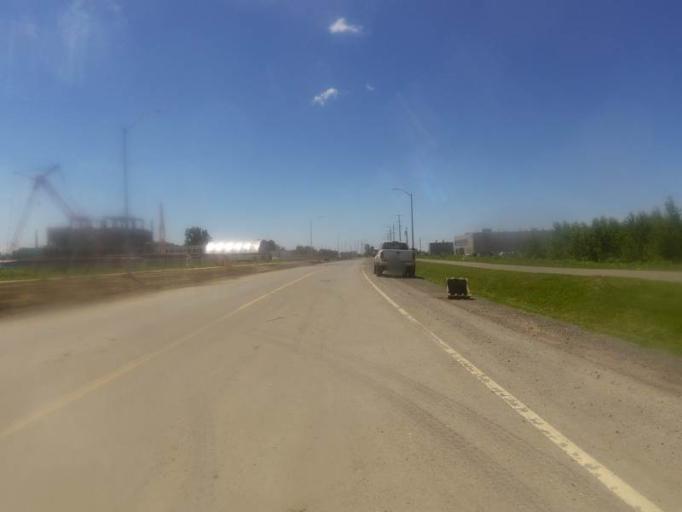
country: CA
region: Ontario
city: Kingston
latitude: 44.2763
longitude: -76.5596
